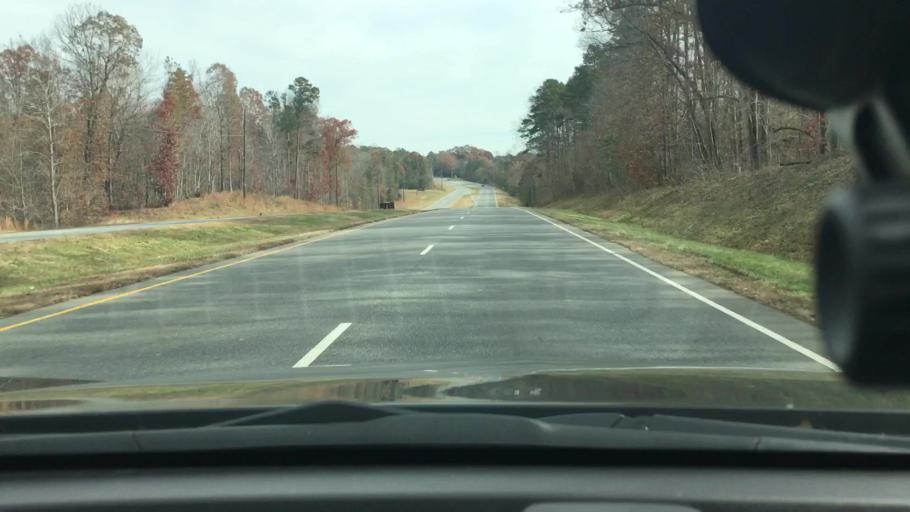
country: US
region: North Carolina
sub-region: Montgomery County
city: Biscoe
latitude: 35.3547
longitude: -79.8208
